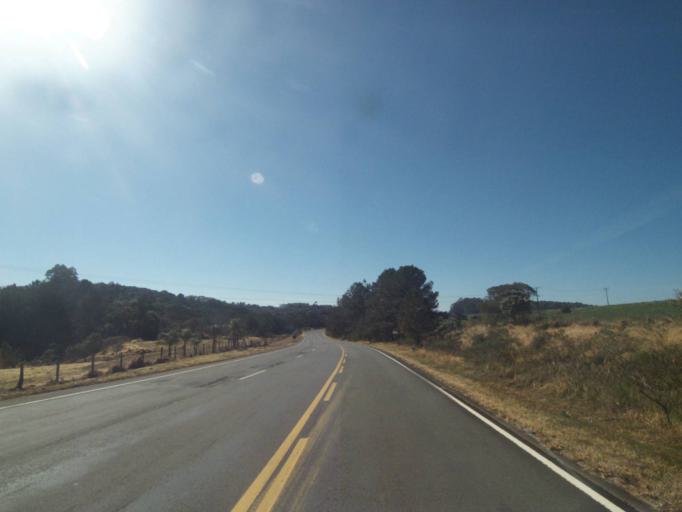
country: BR
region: Parana
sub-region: Tibagi
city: Tibagi
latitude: -24.4684
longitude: -50.4996
